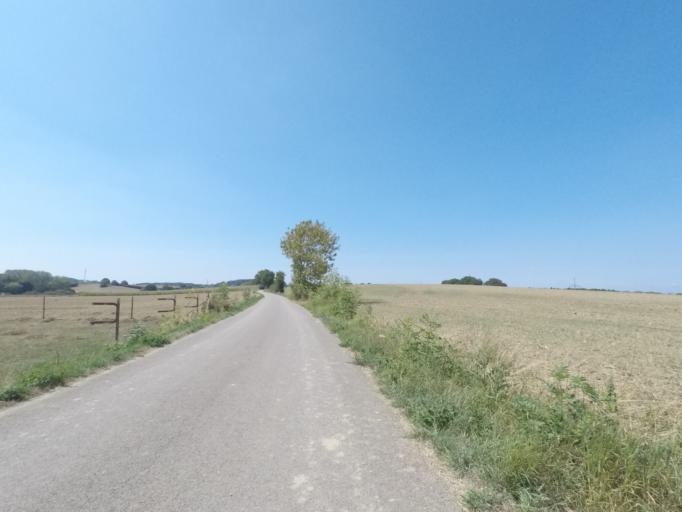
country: LU
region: Luxembourg
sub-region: Canton de Capellen
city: Garnich
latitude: 49.6232
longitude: 5.9737
